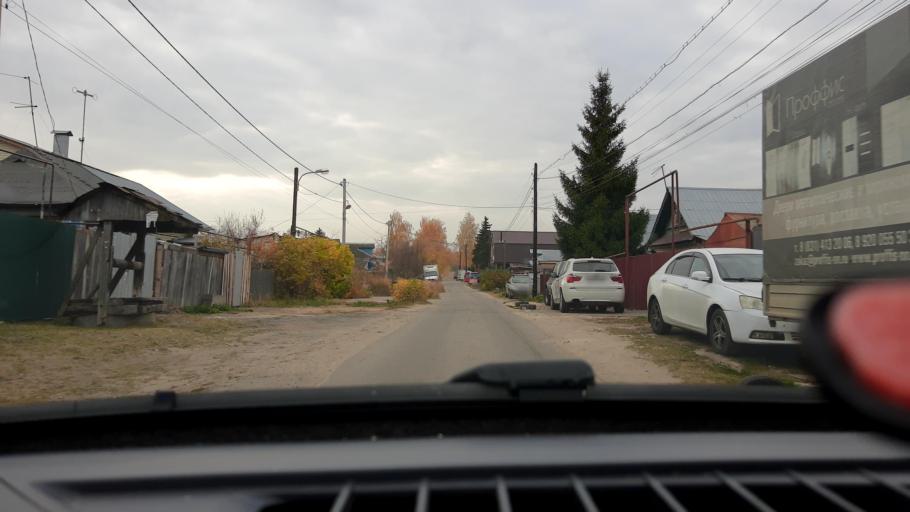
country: RU
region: Nizjnij Novgorod
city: Gorbatovka
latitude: 56.3309
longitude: 43.8333
